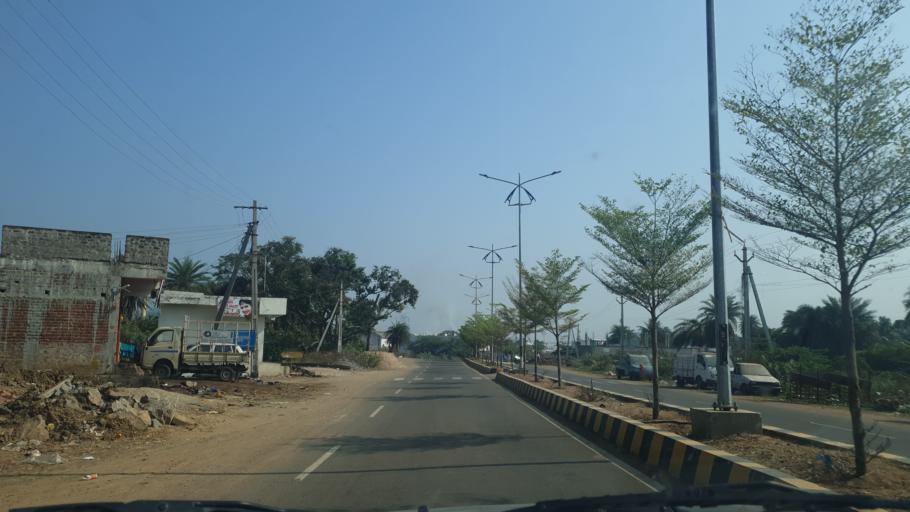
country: IN
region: Andhra Pradesh
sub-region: Srikakulam
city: Tekkali
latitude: 18.6127
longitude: 84.2351
